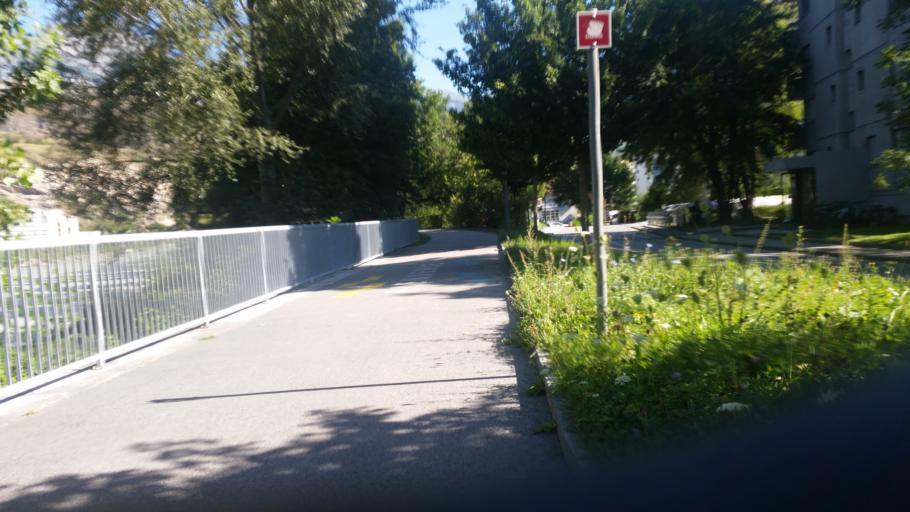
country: CH
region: Valais
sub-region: Sion District
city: Sitten
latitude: 46.2285
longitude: 7.3704
